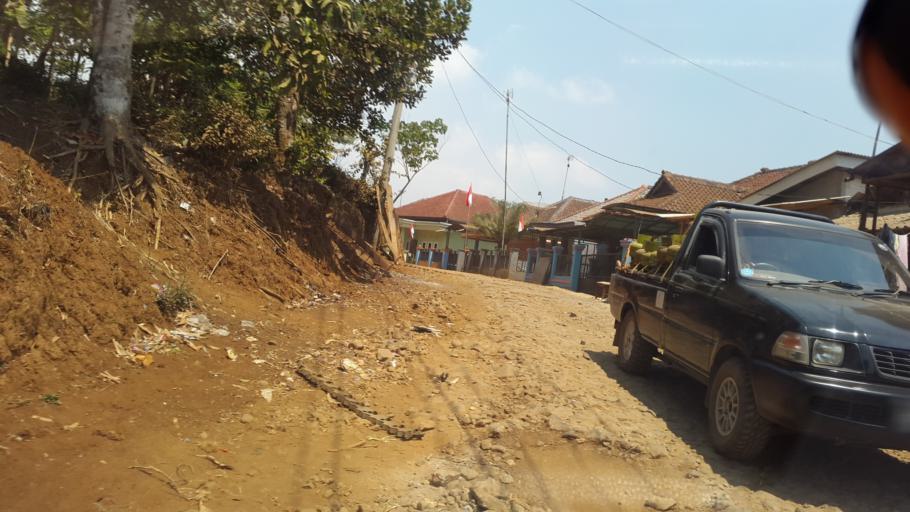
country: ID
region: West Java
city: Cigaru
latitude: -7.0968
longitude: 106.5745
